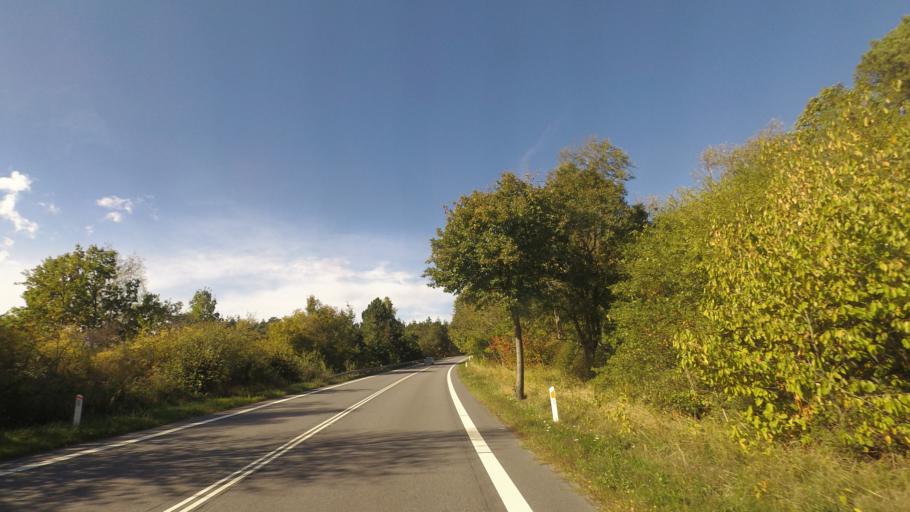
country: DK
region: Capital Region
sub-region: Bornholm Kommune
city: Ronne
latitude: 55.0810
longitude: 14.7545
